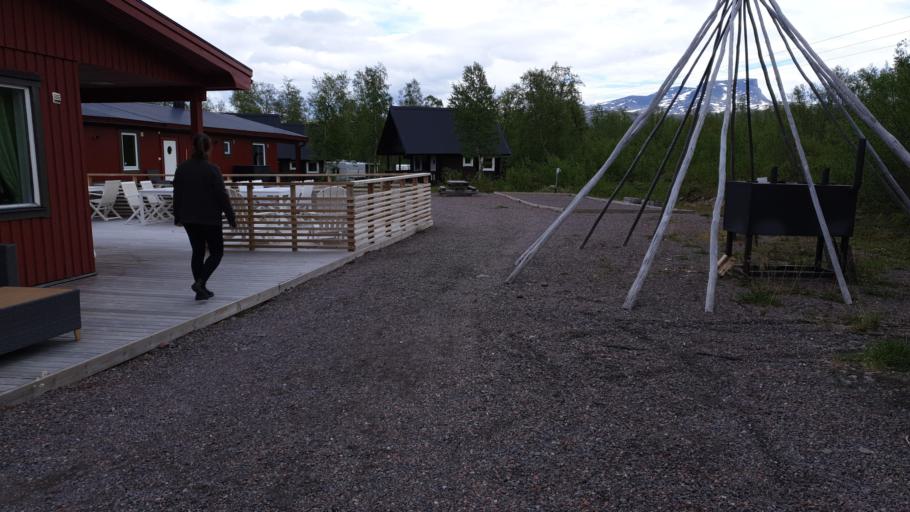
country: NO
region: Troms
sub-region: Bardu
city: Setermoen
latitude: 68.3467
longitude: 18.8323
